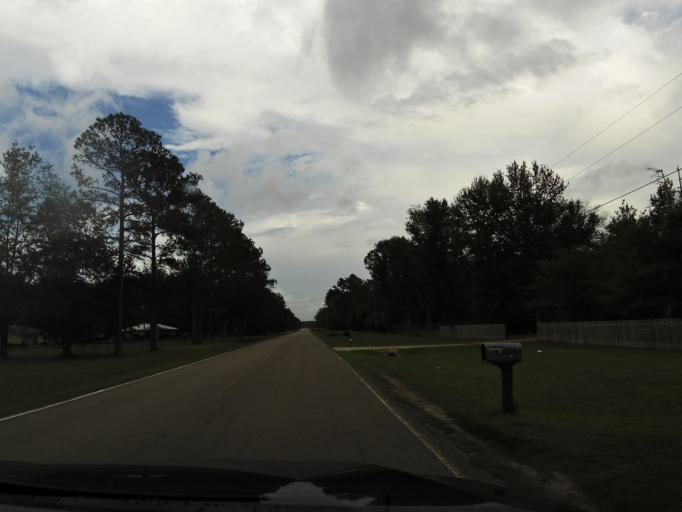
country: US
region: Florida
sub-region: Duval County
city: Baldwin
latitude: 30.4047
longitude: -82.0185
